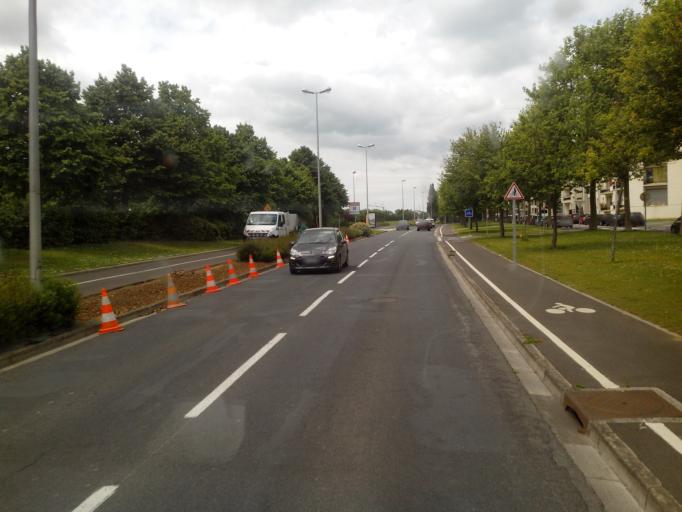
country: FR
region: Lower Normandy
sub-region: Departement du Calvados
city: Saint-Contest
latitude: 49.1989
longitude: -0.3844
